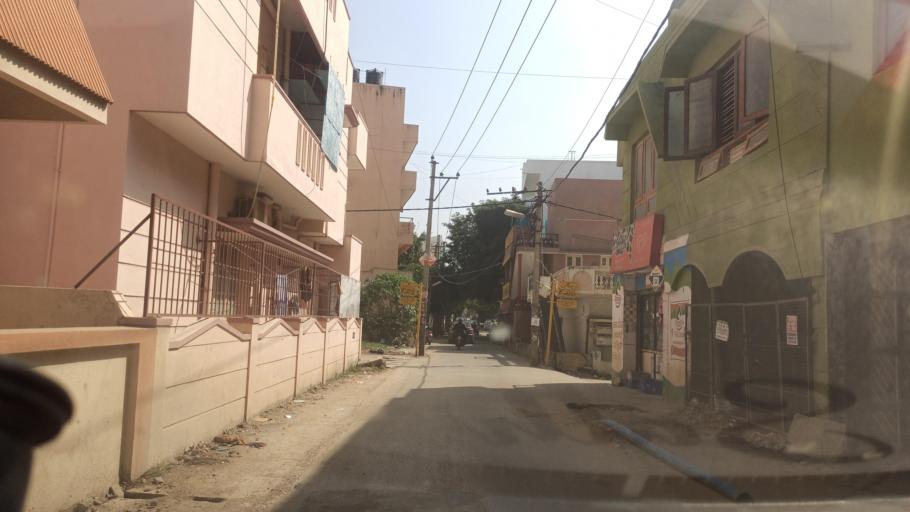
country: IN
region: Karnataka
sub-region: Bangalore Urban
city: Bangalore
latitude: 12.9532
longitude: 77.6949
